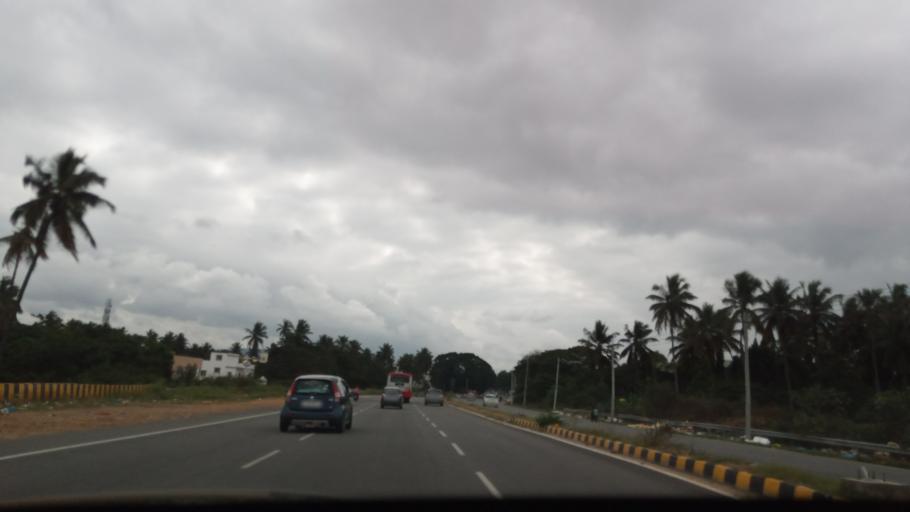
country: IN
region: Karnataka
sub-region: Mysore
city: Mysore
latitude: 12.3414
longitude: 76.6580
